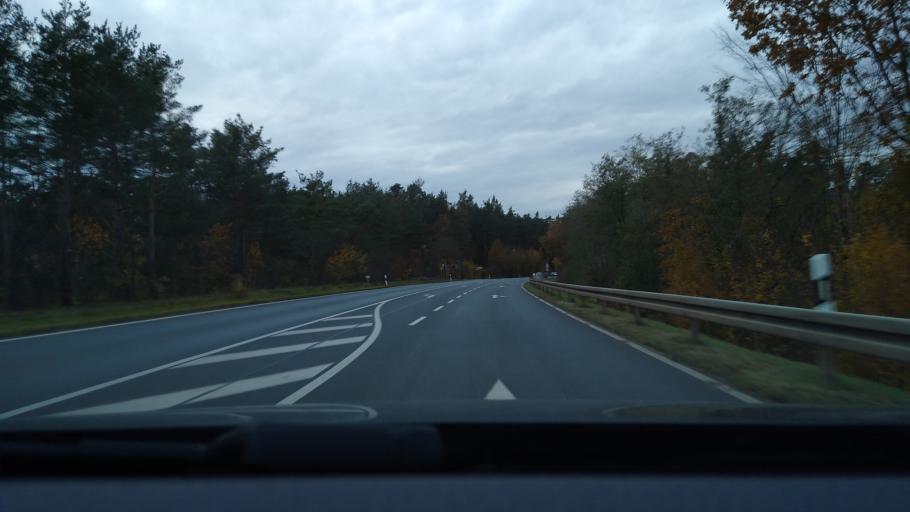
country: DE
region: Bavaria
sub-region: Regierungsbezirk Mittelfranken
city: Rednitzhembach
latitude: 49.3437
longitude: 11.0739
